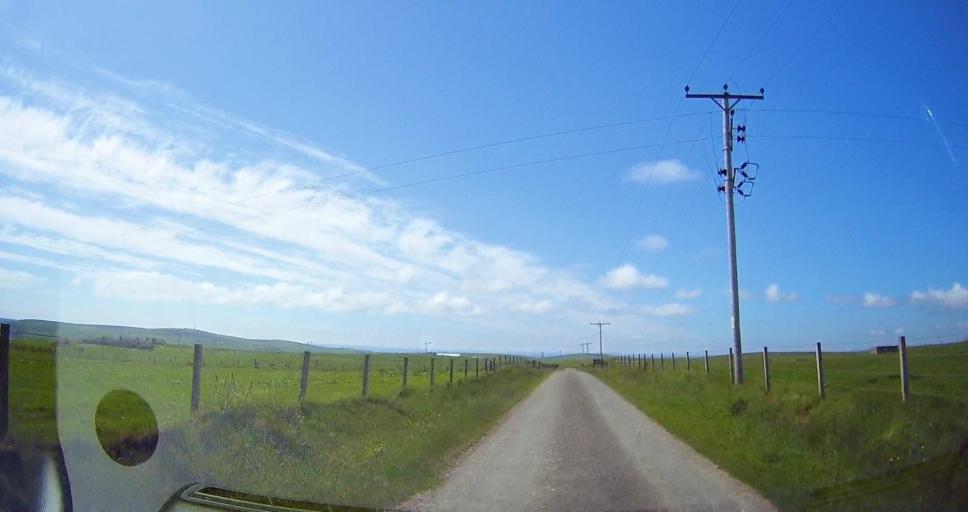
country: GB
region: Scotland
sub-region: Orkney Islands
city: Kirkwall
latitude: 58.8136
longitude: -2.9217
